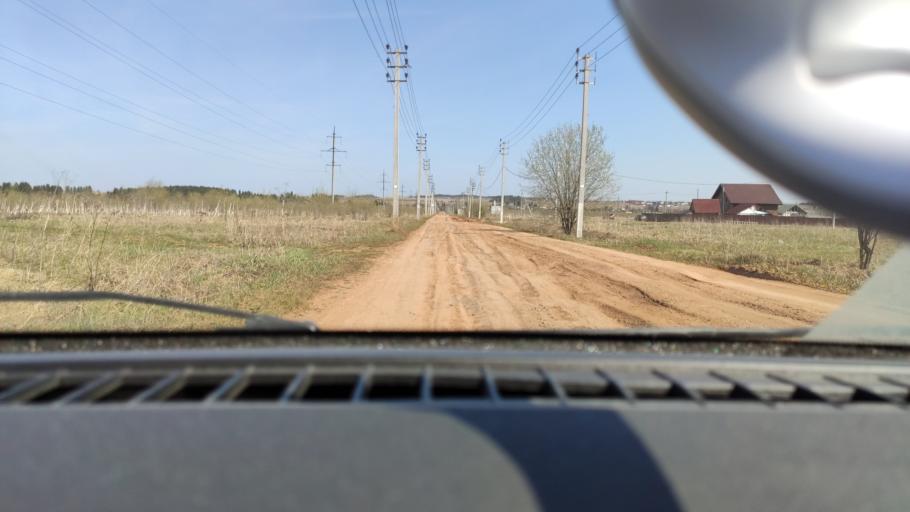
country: RU
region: Perm
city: Kultayevo
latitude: 57.8856
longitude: 55.8548
